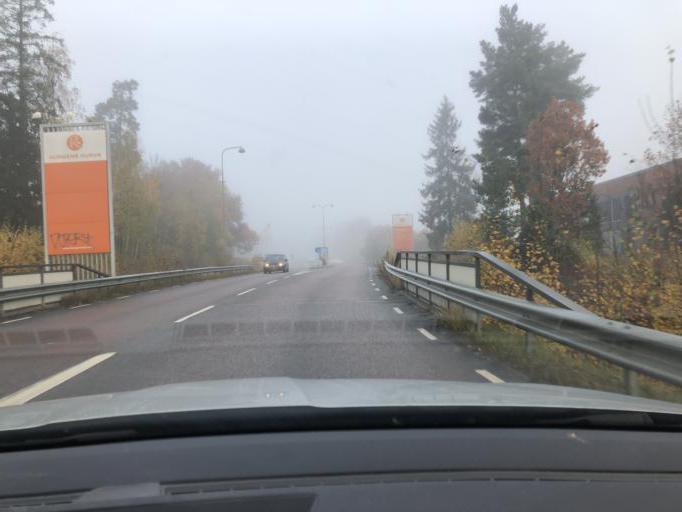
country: SE
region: Stockholm
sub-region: Huddinge Kommun
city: Segeltorp
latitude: 59.2660
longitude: 17.9262
